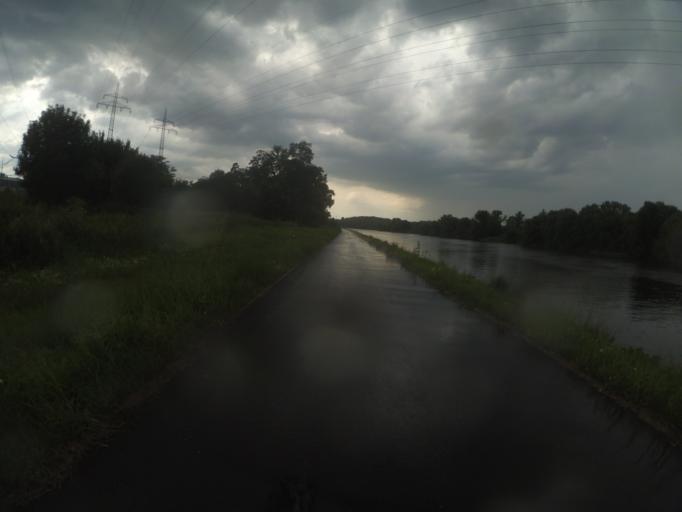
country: CZ
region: Central Bohemia
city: Dolni Berkovice
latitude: 50.4149
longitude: 14.4248
